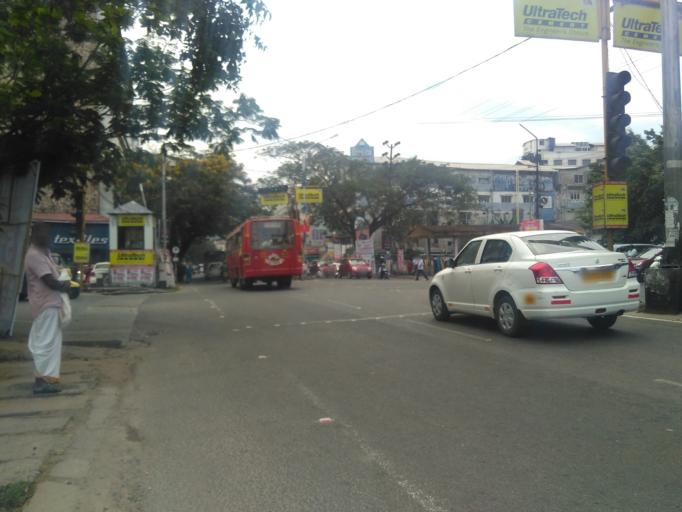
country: IN
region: Kerala
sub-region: Ernakulam
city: Cochin
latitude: 9.9686
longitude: 76.2861
